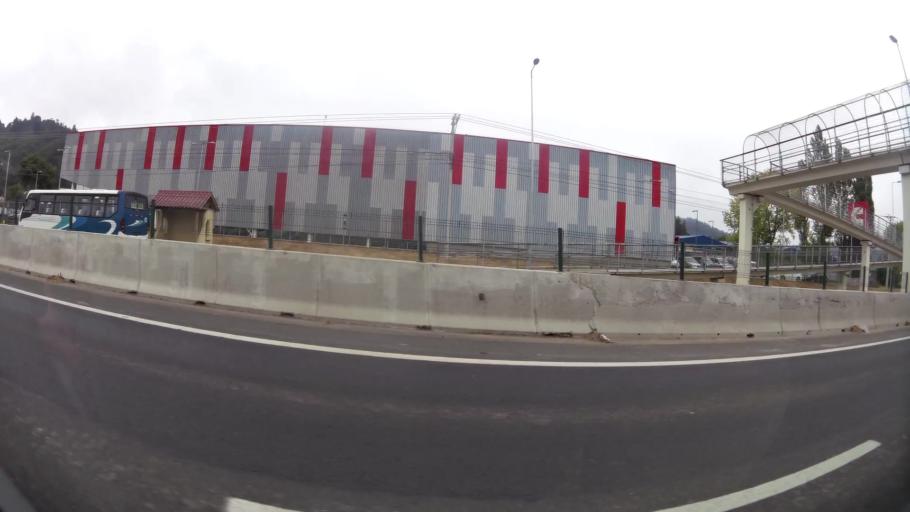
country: CL
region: Biobio
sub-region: Provincia de Concepcion
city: Concepcion
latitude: -36.8195
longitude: -73.0050
